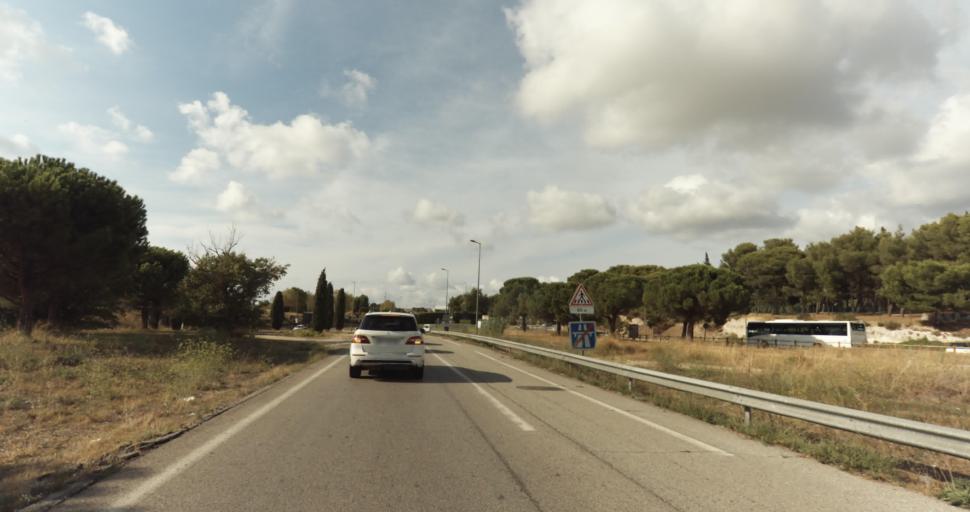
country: FR
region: Provence-Alpes-Cote d'Azur
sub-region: Departement des Bouches-du-Rhone
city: Vitrolles
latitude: 43.4430
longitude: 5.2464
